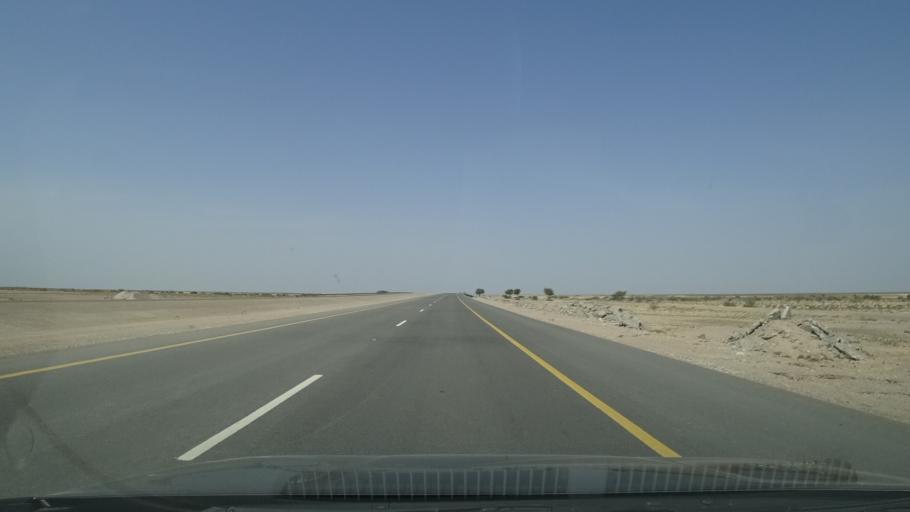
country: OM
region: Muhafazat ad Dakhiliyah
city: Adam
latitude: 21.8282
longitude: 57.3780
